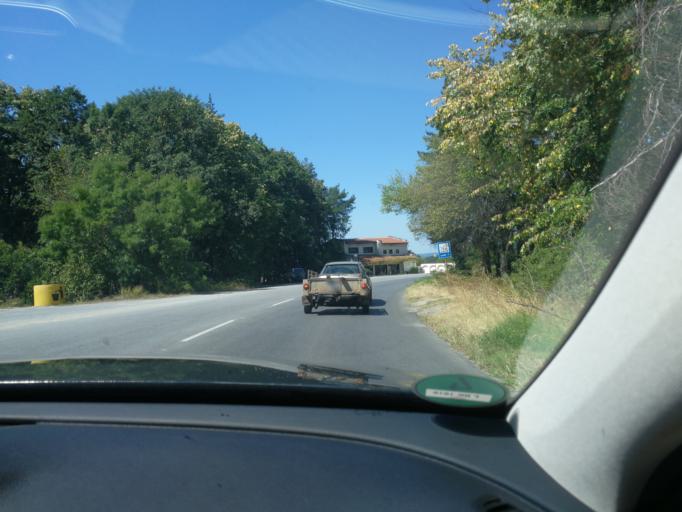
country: BG
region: Khaskovo
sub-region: Obshtina Topolovgrad
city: Topolovgrad
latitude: 42.0774
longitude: 26.3241
